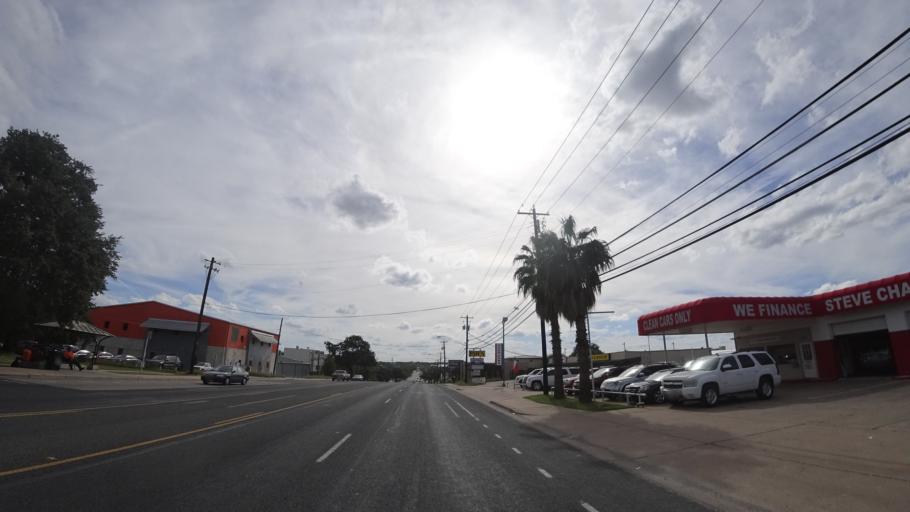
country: US
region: Texas
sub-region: Travis County
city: Austin
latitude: 30.2147
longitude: -97.7692
